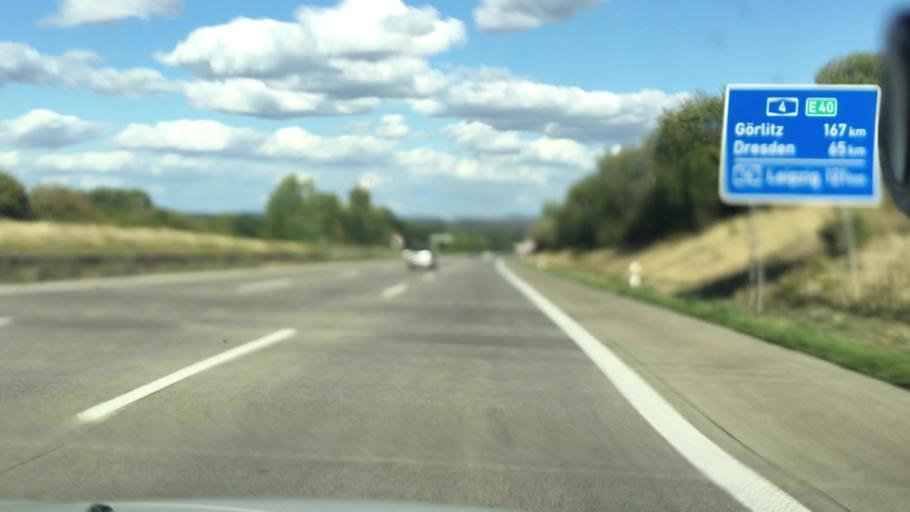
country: DE
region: Saxony
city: Frankenberg
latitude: 50.9111
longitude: 12.9865
